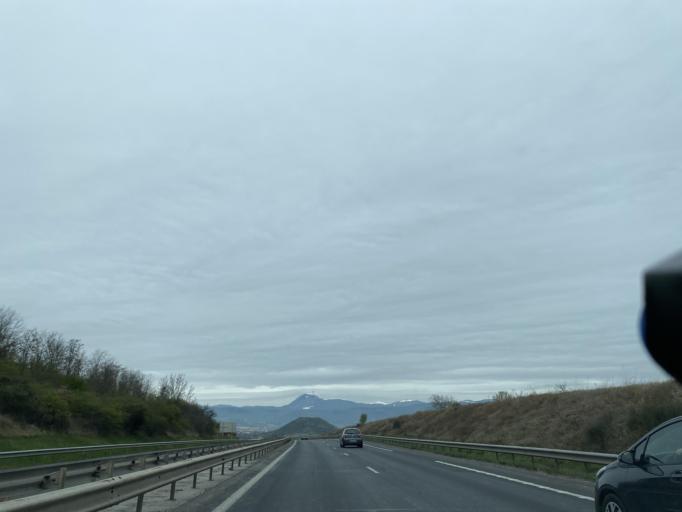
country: FR
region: Auvergne
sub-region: Departement du Puy-de-Dome
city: Aulnat
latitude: 45.7731
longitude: 3.1647
